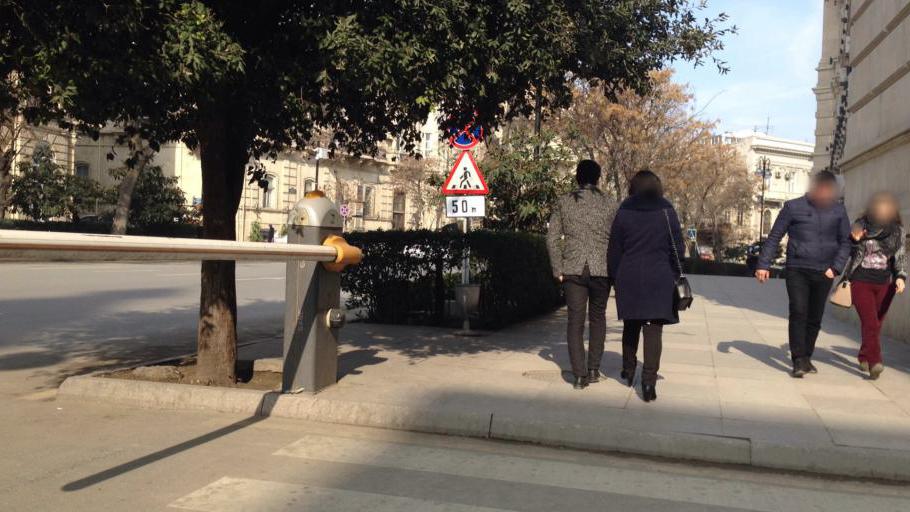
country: AZ
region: Baki
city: Badamdar
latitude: 40.3672
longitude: 49.8315
